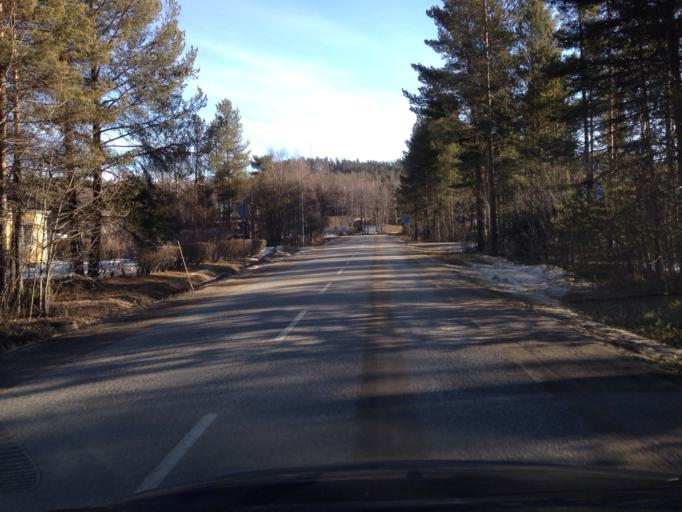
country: SE
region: Jaemtland
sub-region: Harjedalens Kommun
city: Sveg
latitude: 62.1557
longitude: 13.8887
